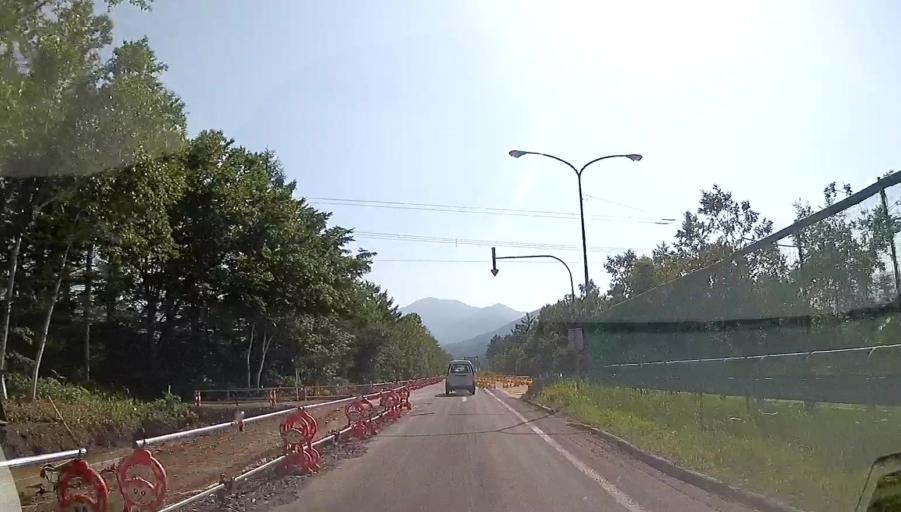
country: JP
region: Hokkaido
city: Otofuke
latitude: 42.9795
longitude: 142.8300
